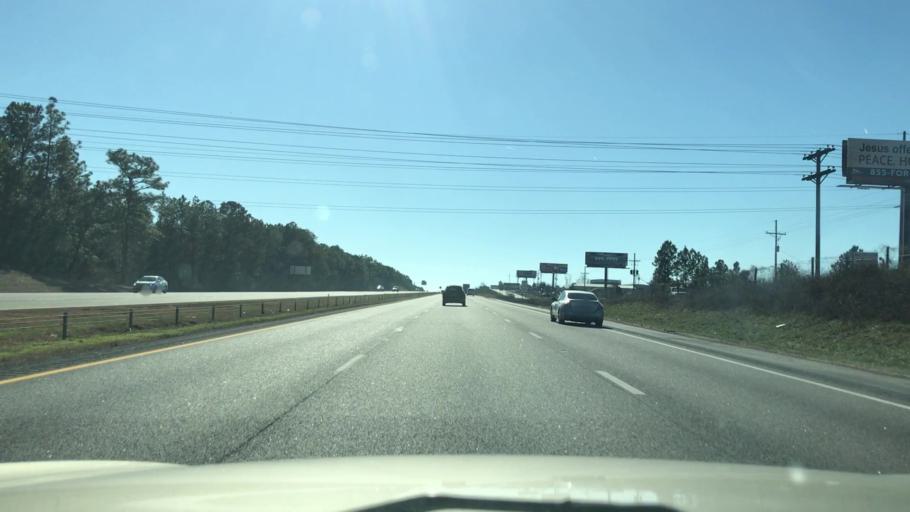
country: US
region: South Carolina
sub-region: Lexington County
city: Pineridge
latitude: 33.8714
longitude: -81.0349
